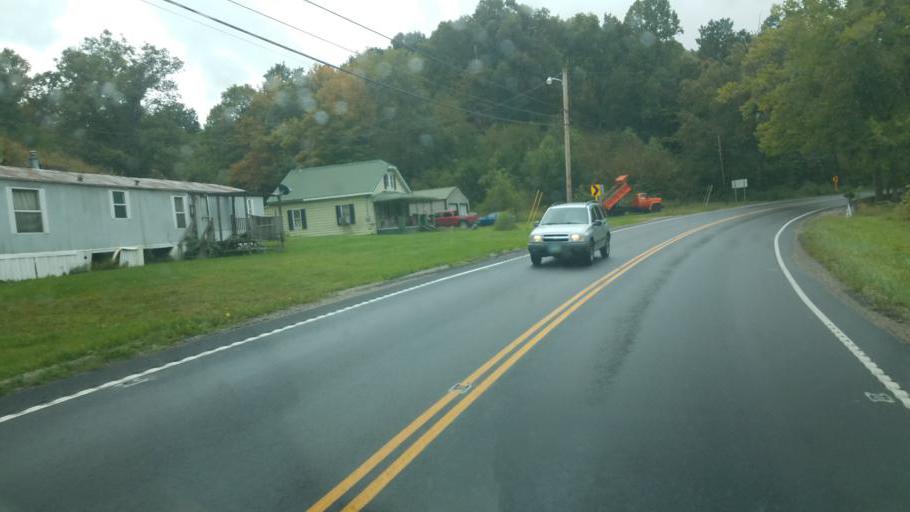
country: US
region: Ohio
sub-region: Scioto County
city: Wheelersburg
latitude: 38.7880
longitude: -82.7711
